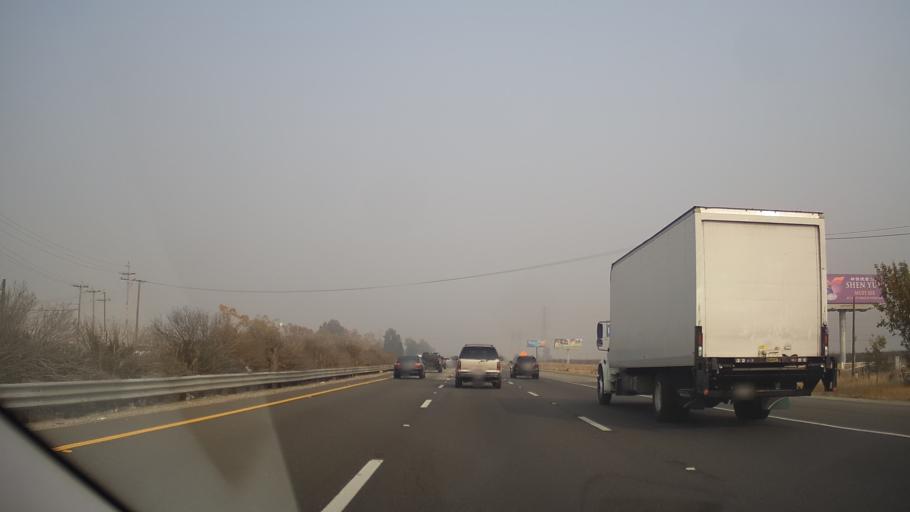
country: US
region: California
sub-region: Solano County
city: Hartley
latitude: 38.3946
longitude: -121.9244
